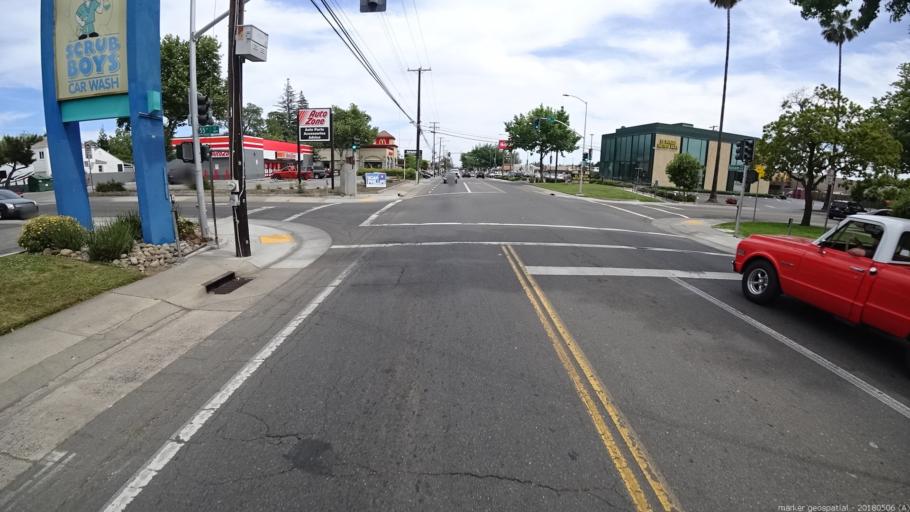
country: US
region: California
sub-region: Sacramento County
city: Sacramento
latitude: 38.5587
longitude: -121.4393
